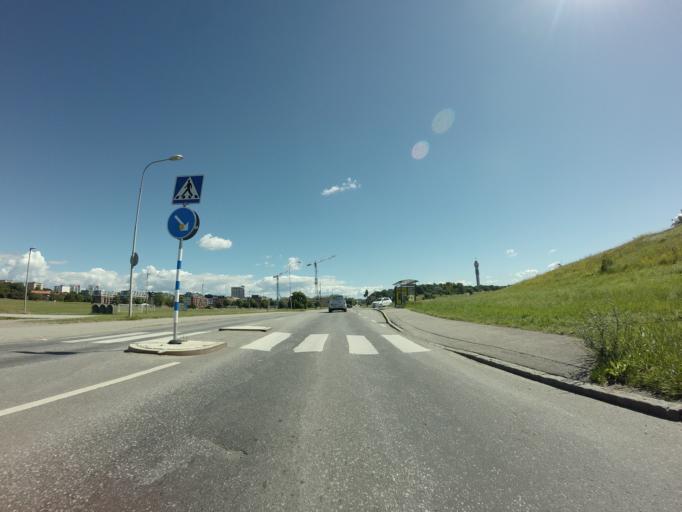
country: SE
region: Stockholm
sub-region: Stockholms Kommun
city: OEstermalm
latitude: 59.3400
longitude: 18.1060
